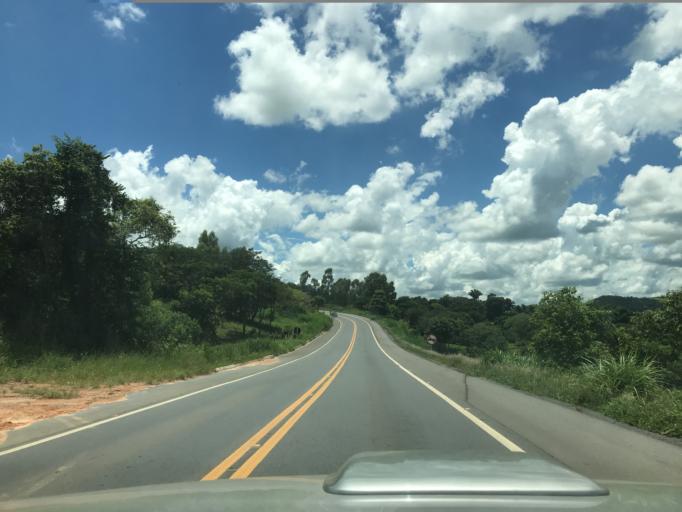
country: BR
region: Minas Gerais
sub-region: Perdoes
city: Perdoes
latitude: -21.0895
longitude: -45.0984
